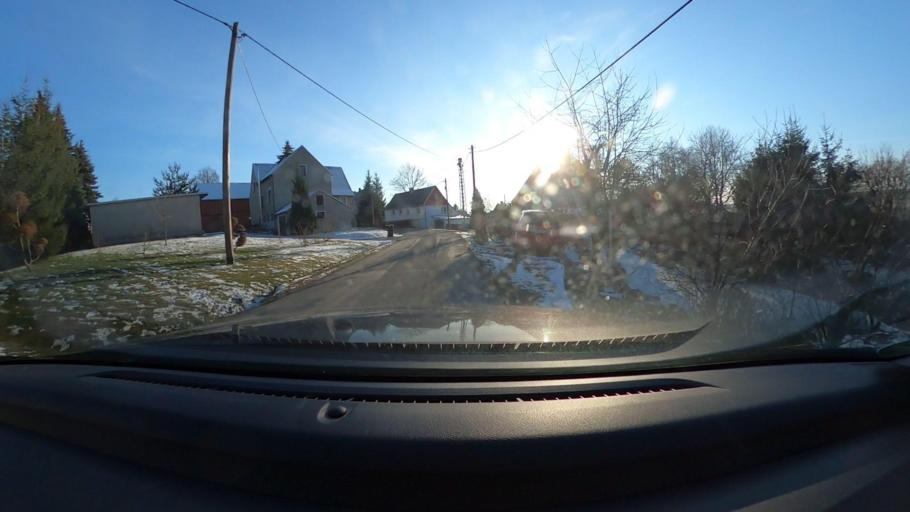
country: DE
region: Saxony
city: Frankenstein
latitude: 50.9425
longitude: 13.2186
